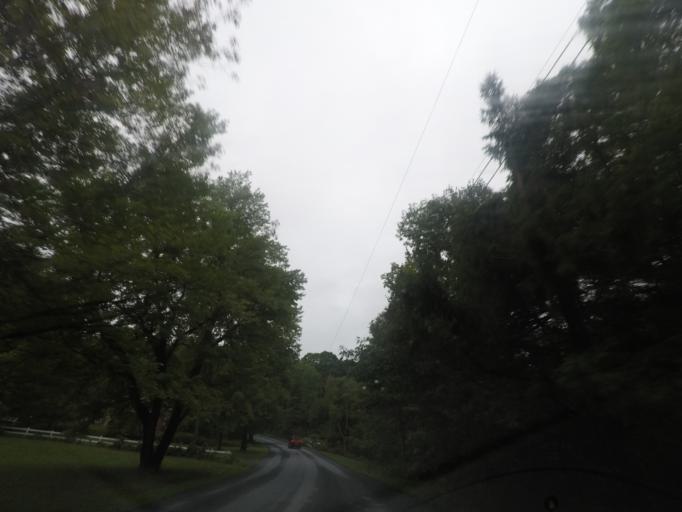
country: US
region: New York
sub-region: Rensselaer County
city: West Sand Lake
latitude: 42.6124
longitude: -73.6403
